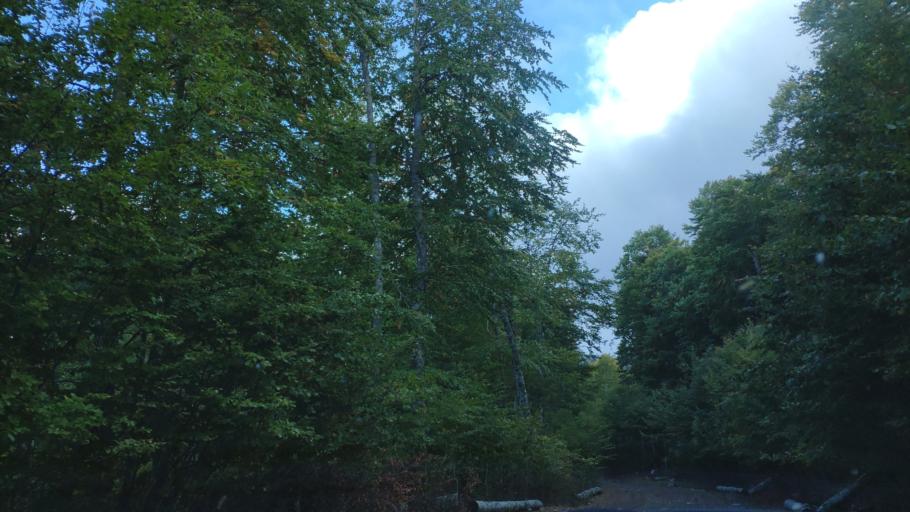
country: GR
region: West Macedonia
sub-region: Nomos Kastorias
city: Nestorio
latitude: 40.3119
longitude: 20.9151
